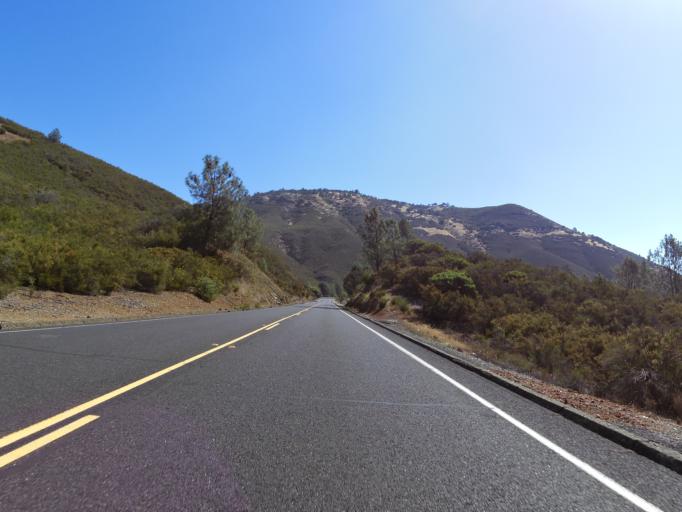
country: US
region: California
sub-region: Tuolumne County
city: Tuolumne City
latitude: 37.7069
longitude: -120.2490
